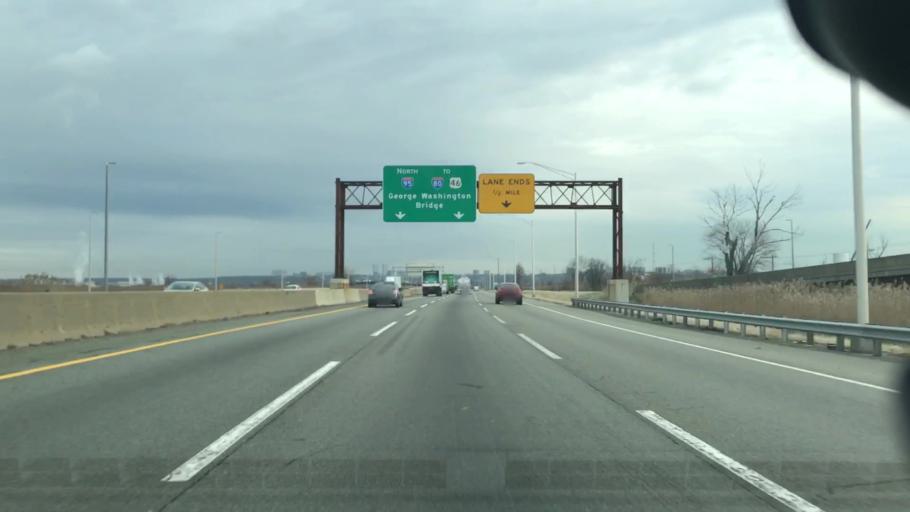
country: US
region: New Jersey
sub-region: Hudson County
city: Secaucus
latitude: 40.8139
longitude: -74.0551
